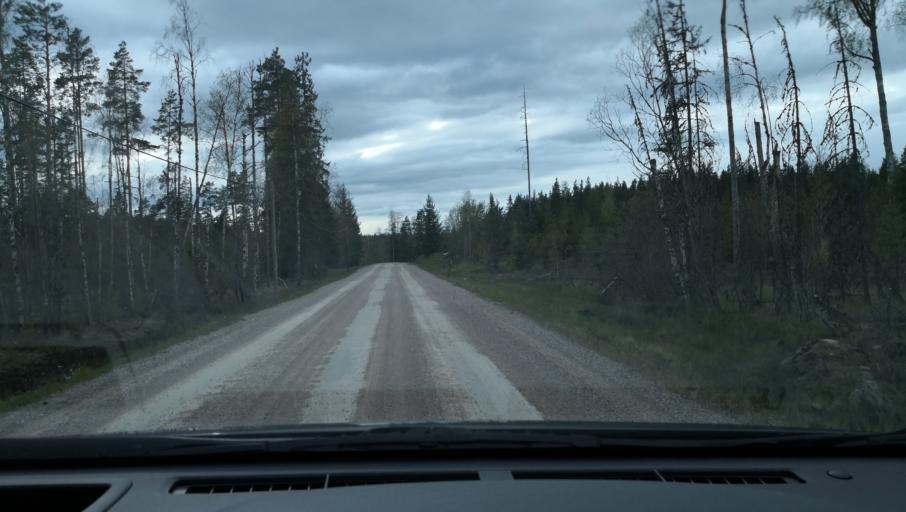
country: SE
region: Vaestmanland
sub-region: Fagersta Kommun
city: Fagersta
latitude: 60.0908
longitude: 15.8217
